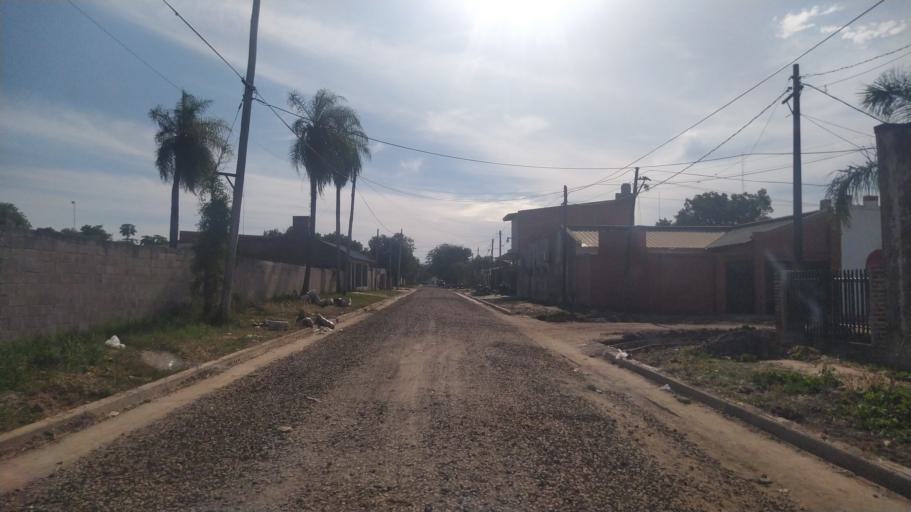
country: AR
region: Corrientes
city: Corrientes
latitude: -27.4880
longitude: -58.8123
